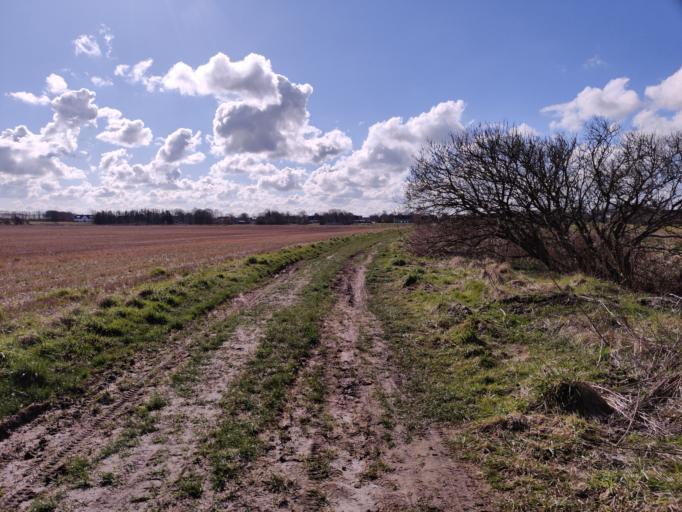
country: DK
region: North Denmark
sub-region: Alborg Kommune
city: Frejlev
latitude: 57.0429
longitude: 9.7414
